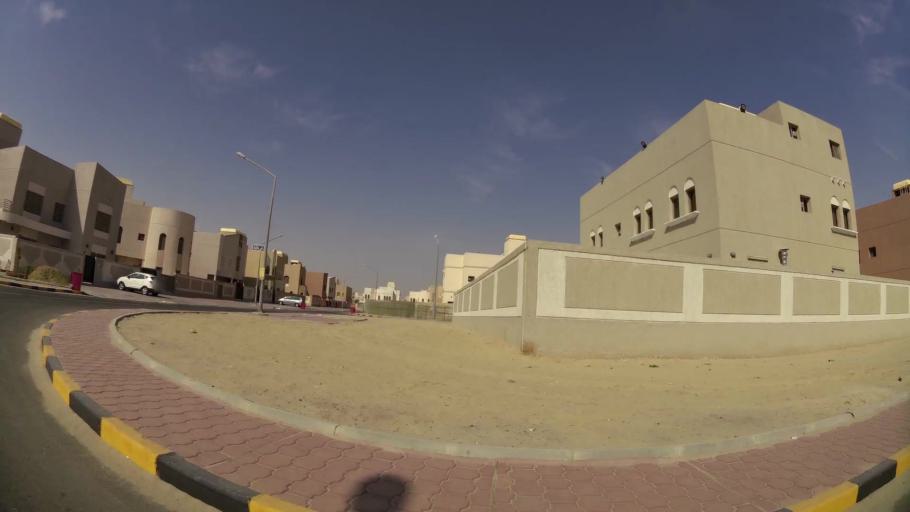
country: KW
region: Al Ahmadi
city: Al Wafrah
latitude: 28.7965
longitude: 48.0743
